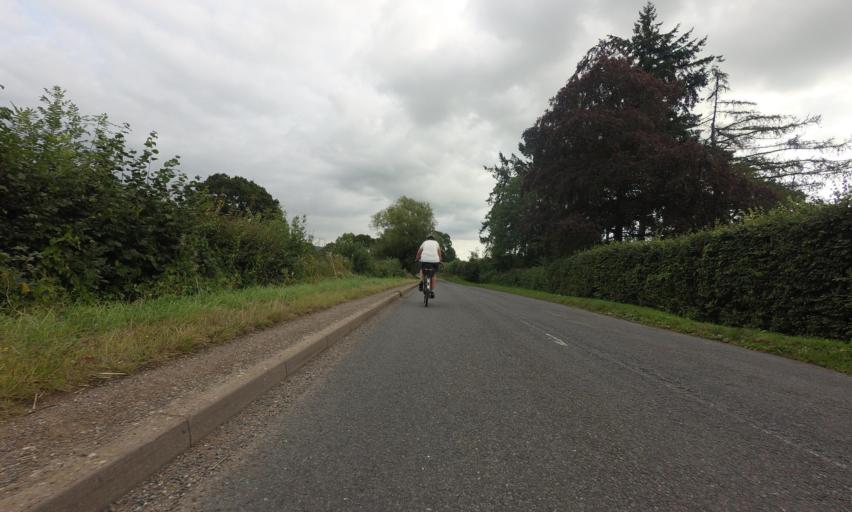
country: GB
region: England
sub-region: Gloucestershire
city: Winchcombe
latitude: 51.9668
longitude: -1.9723
